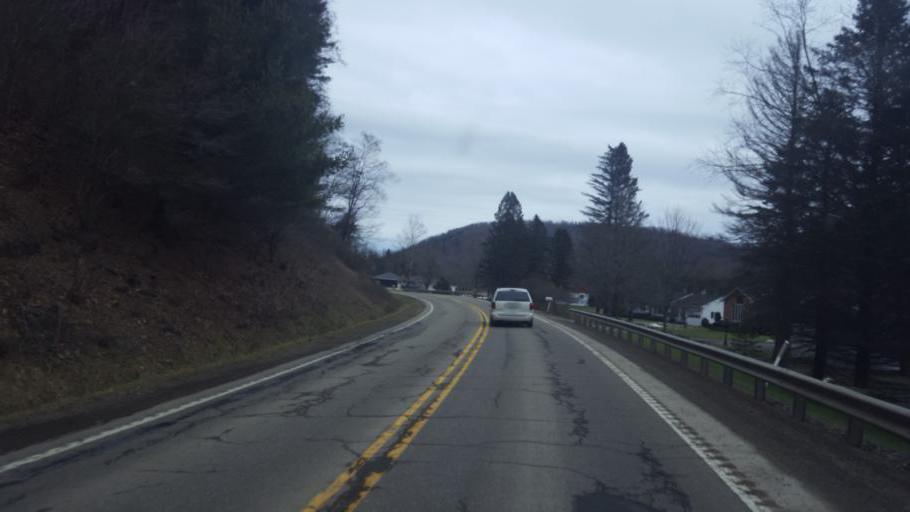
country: US
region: Pennsylvania
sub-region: Potter County
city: Coudersport
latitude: 41.8124
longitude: -77.9940
